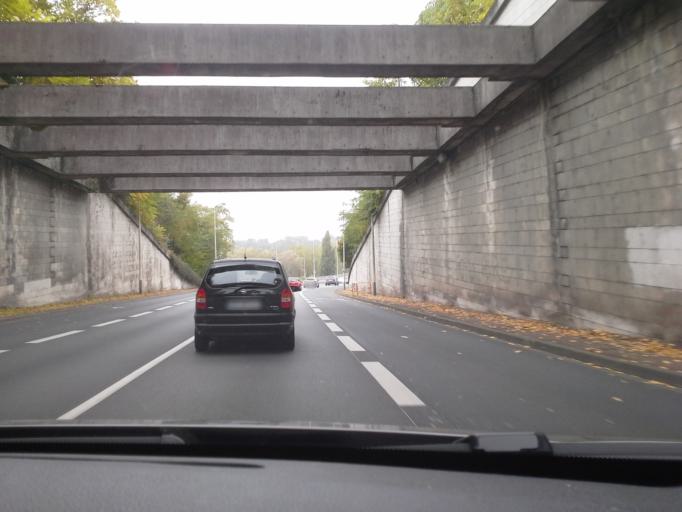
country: FR
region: Centre
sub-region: Departement d'Indre-et-Loire
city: Tours
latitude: 47.4049
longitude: 0.7028
